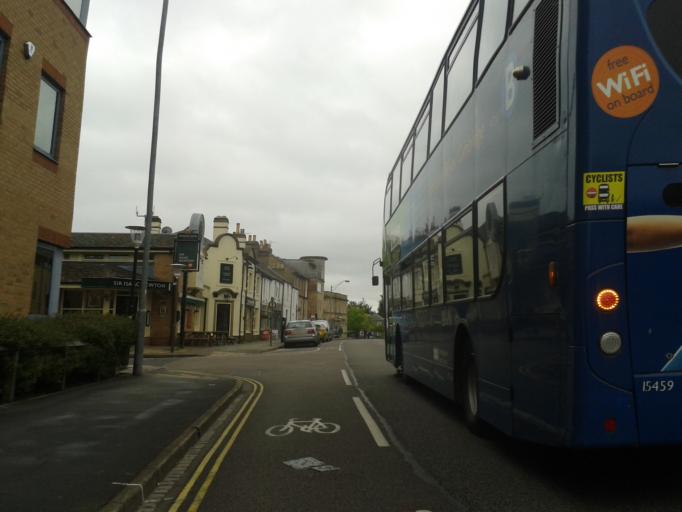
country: GB
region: England
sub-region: Cambridgeshire
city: Cambridge
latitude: 52.2136
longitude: 0.1116
